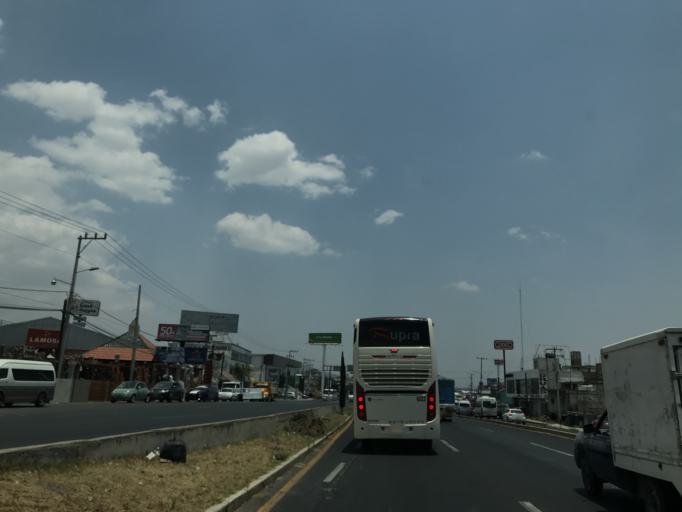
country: MX
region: Tlaxcala
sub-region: Yauhquemehcan
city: Hualcaltzinco
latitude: 19.4143
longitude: -98.1616
